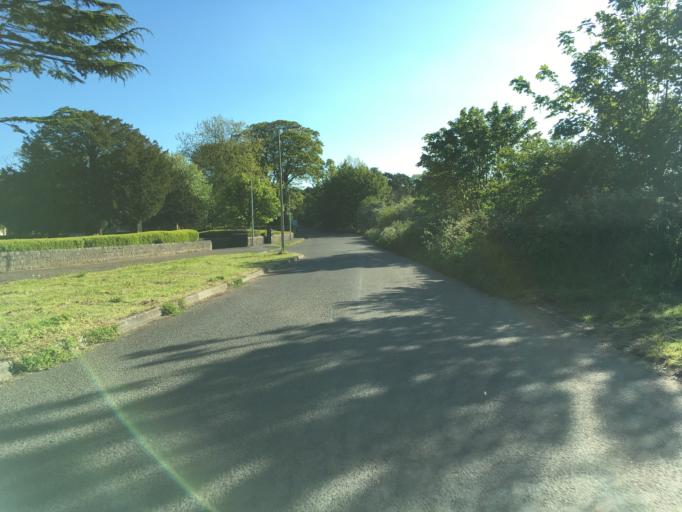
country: GB
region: England
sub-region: North Somerset
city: Long Ashton
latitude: 51.4221
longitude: -2.6943
